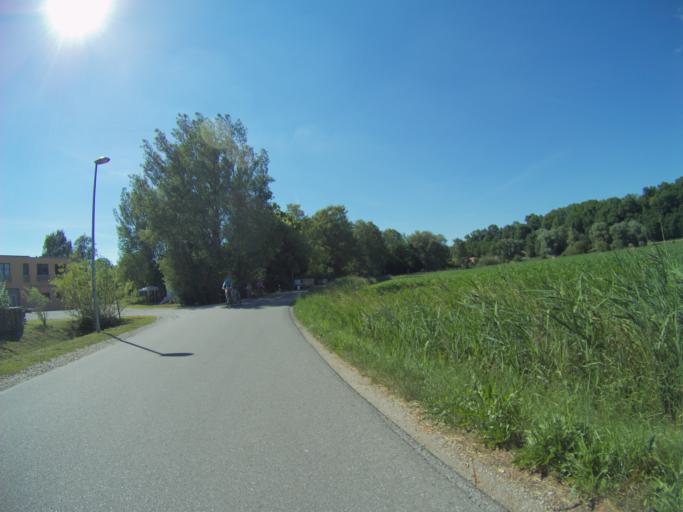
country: DE
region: Bavaria
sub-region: Upper Bavaria
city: Freising
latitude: 48.3912
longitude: 11.7261
